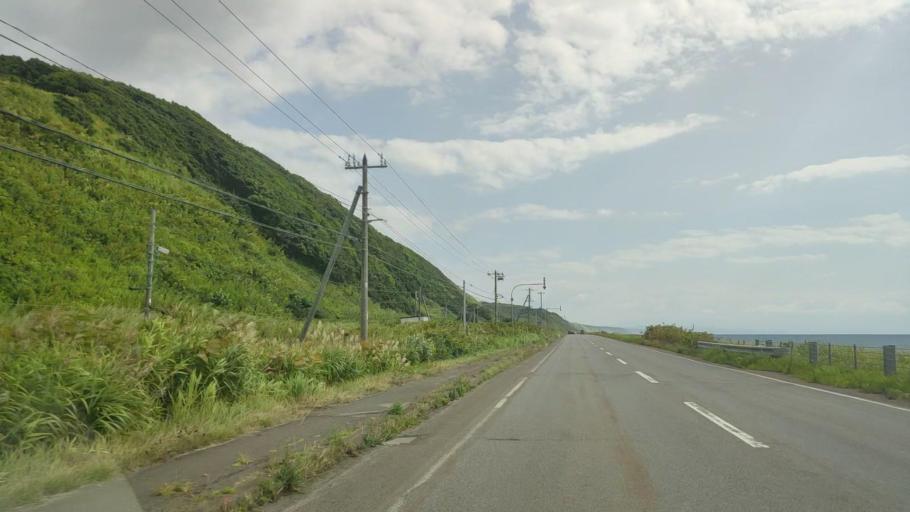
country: JP
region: Hokkaido
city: Rumoi
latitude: 44.1097
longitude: 141.6590
